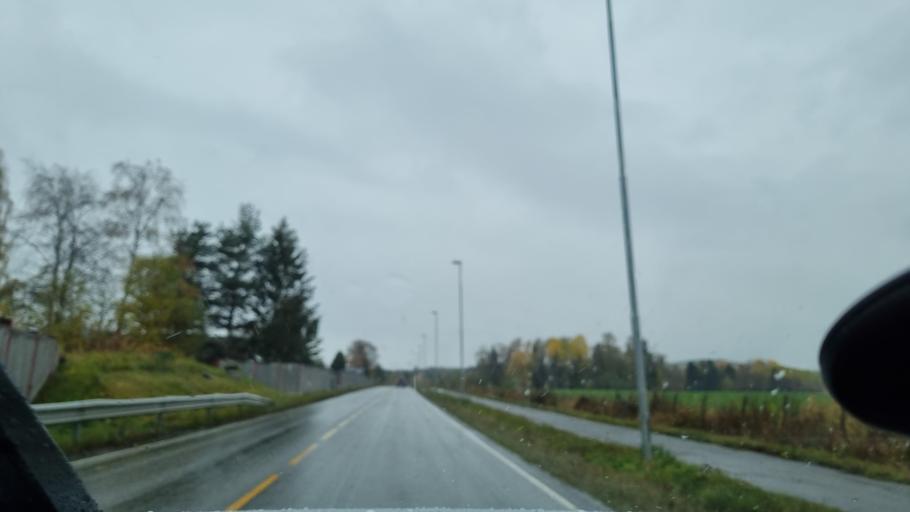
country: NO
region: Hedmark
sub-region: Hamar
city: Hamar
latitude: 60.8279
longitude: 11.0664
